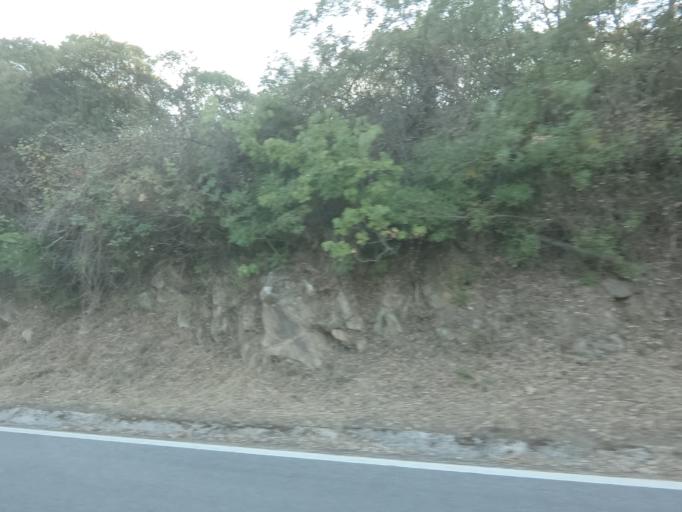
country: PT
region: Viseu
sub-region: Tabuaco
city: Tabuaco
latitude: 41.1316
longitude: -7.5714
